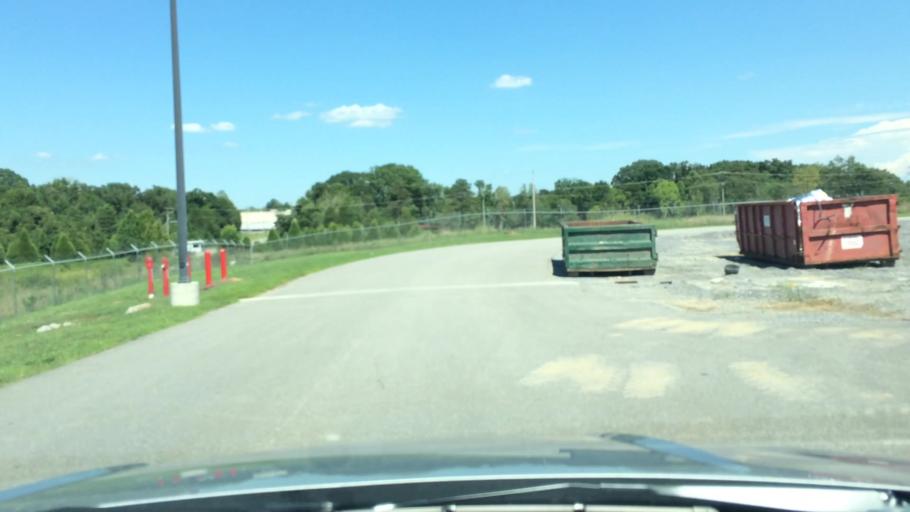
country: US
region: Tennessee
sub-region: McMinn County
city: Athens
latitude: 35.4786
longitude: -84.6431
